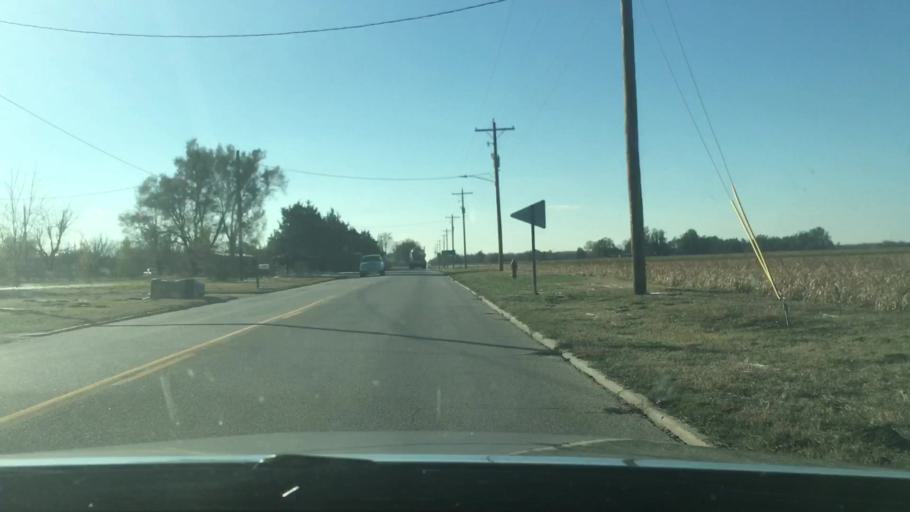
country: US
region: Kansas
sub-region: Reno County
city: Nickerson
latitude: 38.1448
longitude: -98.0907
